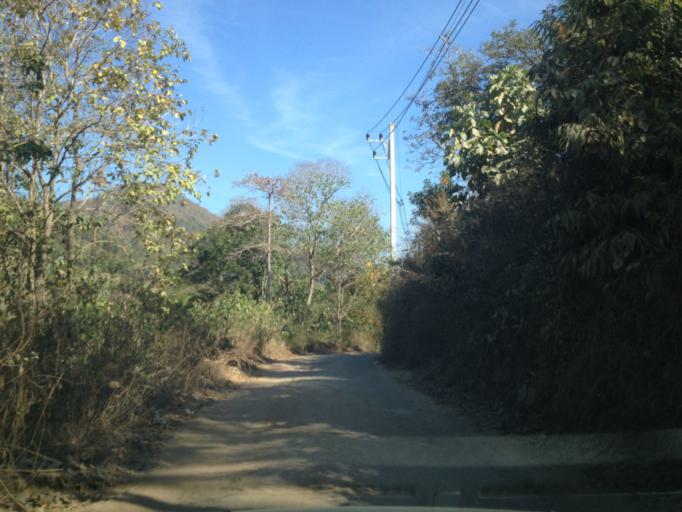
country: TH
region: Mae Hong Son
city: Ban Huai I Huak
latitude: 18.0786
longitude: 98.1899
